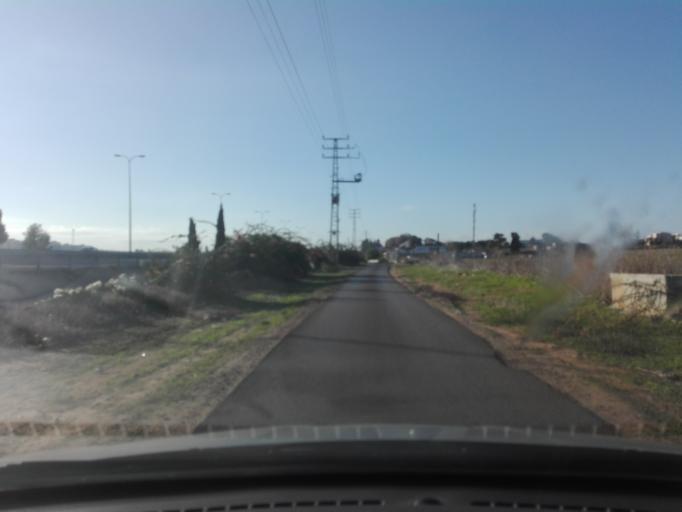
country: IL
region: Central District
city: Netanya
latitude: 32.3072
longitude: 34.8644
